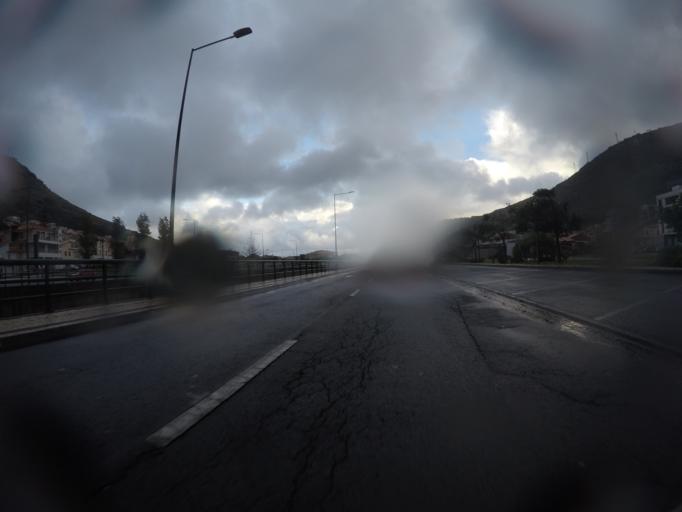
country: PT
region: Madeira
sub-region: Machico
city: Machico
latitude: 32.7224
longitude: -16.7692
